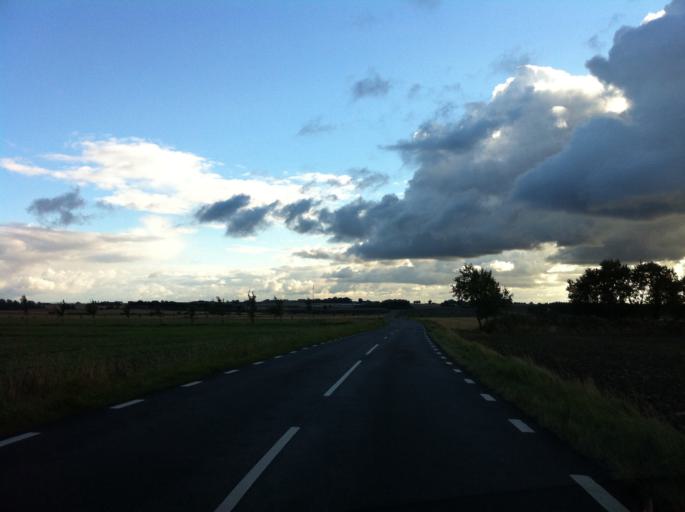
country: SE
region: Skane
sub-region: Svalovs Kommun
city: Svaloev
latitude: 55.9166
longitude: 13.2021
